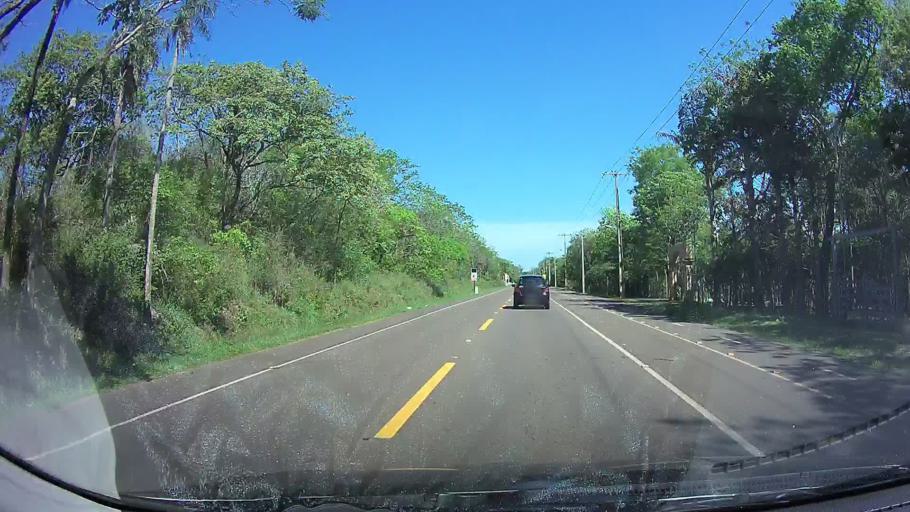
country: PY
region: Cordillera
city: San Bernardino
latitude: -25.2460
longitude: -57.3231
